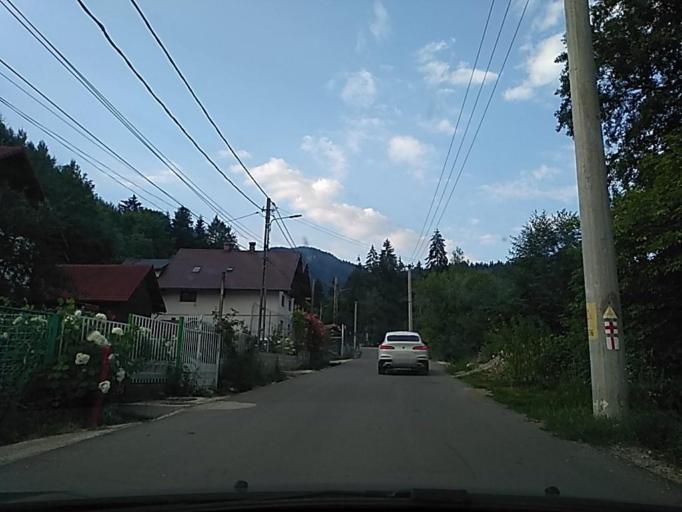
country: RO
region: Brasov
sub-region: Comuna Bran
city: Simon
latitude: 45.4917
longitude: 25.3841
